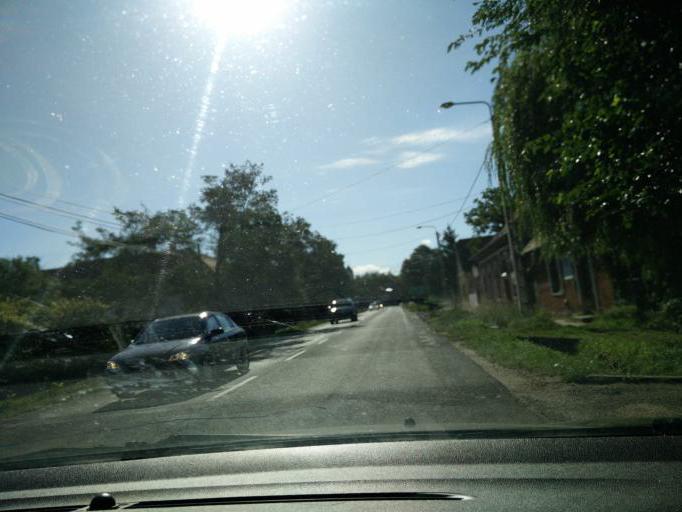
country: HU
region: Pest
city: Piliscsaba
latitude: 47.6344
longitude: 18.8210
